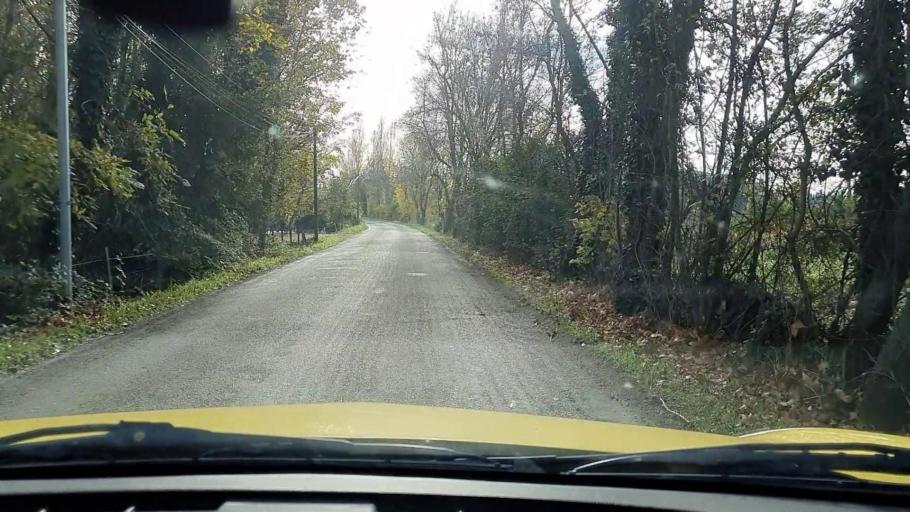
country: FR
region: Languedoc-Roussillon
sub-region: Departement du Gard
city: Meynes
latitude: 43.8588
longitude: 4.5751
